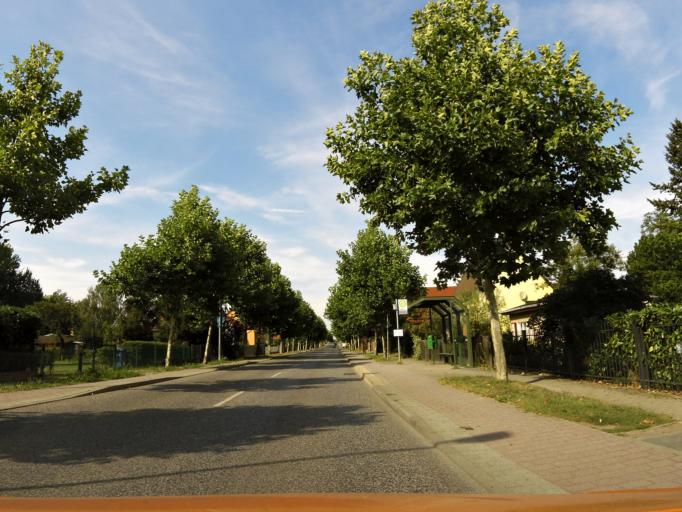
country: DE
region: Brandenburg
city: Teltow
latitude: 52.3824
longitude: 13.2477
